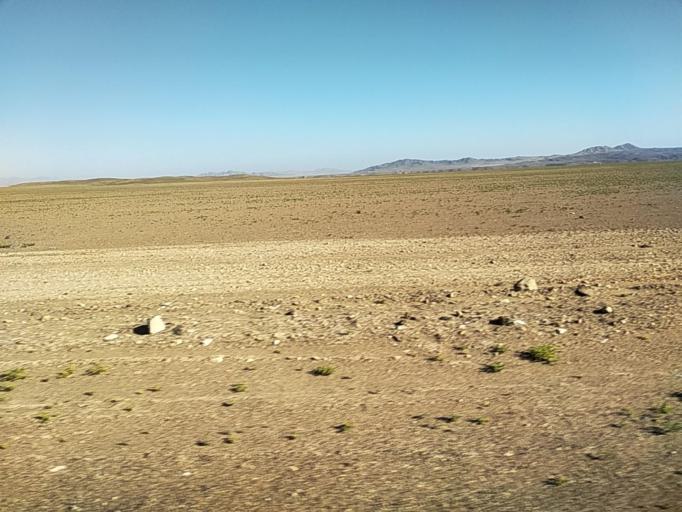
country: CL
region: Atacama
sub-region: Provincia de Copiapo
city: Copiapo
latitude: -27.3198
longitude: -70.7396
